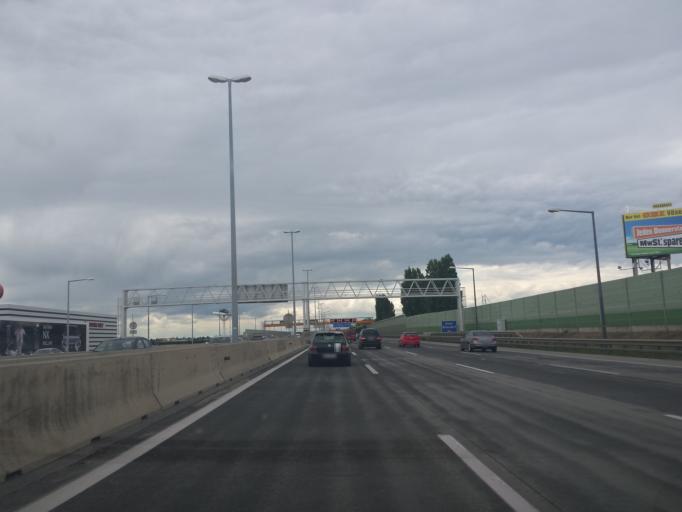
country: AT
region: Lower Austria
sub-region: Politischer Bezirk Modling
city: Vosendorf
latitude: 48.1392
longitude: 16.3327
